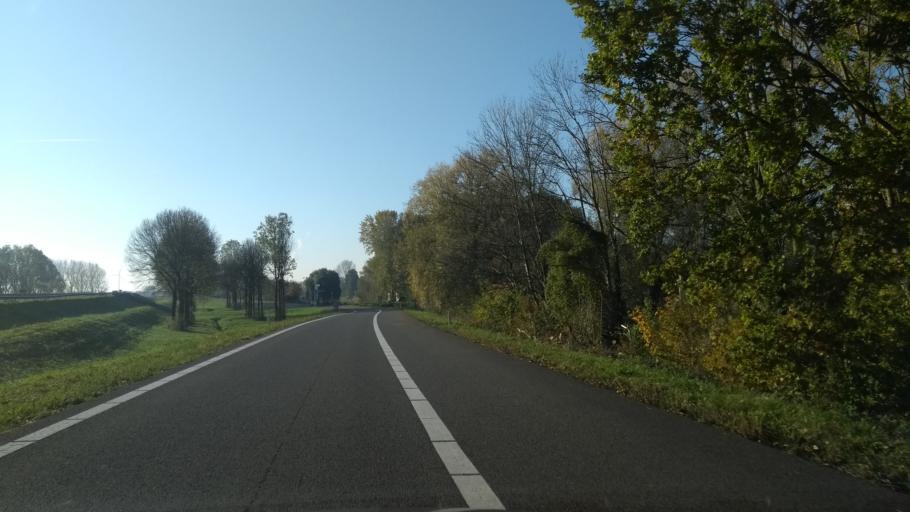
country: NL
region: Gelderland
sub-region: Gemeente Rheden
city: Rheden
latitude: 52.0048
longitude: 6.0410
